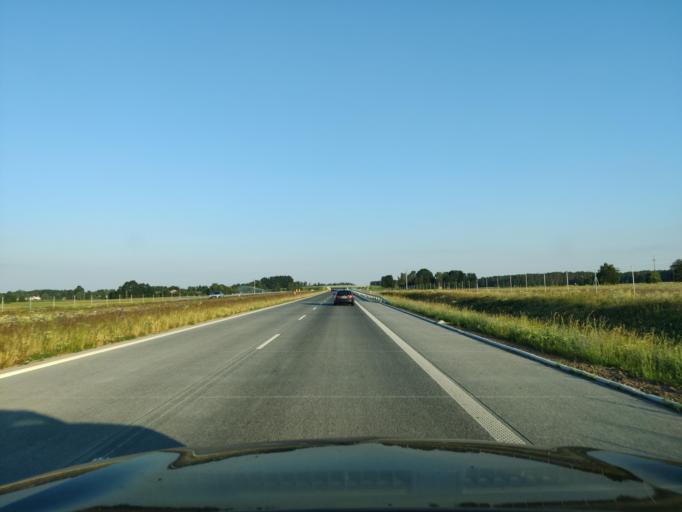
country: PL
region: Masovian Voivodeship
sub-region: Powiat mlawski
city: Strzegowo
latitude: 52.8701
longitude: 20.2807
